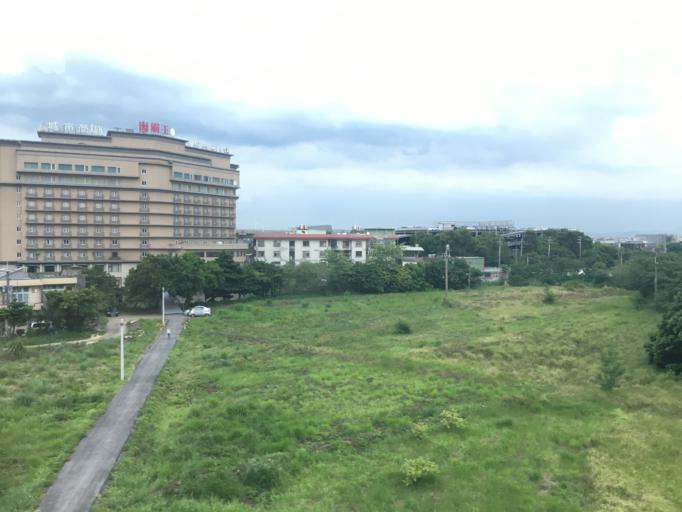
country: TW
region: Taiwan
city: Taoyuan City
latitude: 25.0578
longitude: 121.2102
